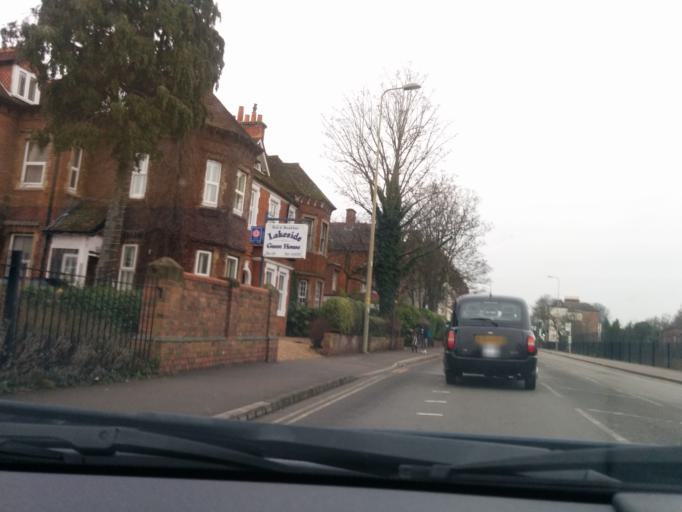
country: GB
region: England
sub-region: Oxfordshire
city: Oxford
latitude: 51.7410
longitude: -1.2545
